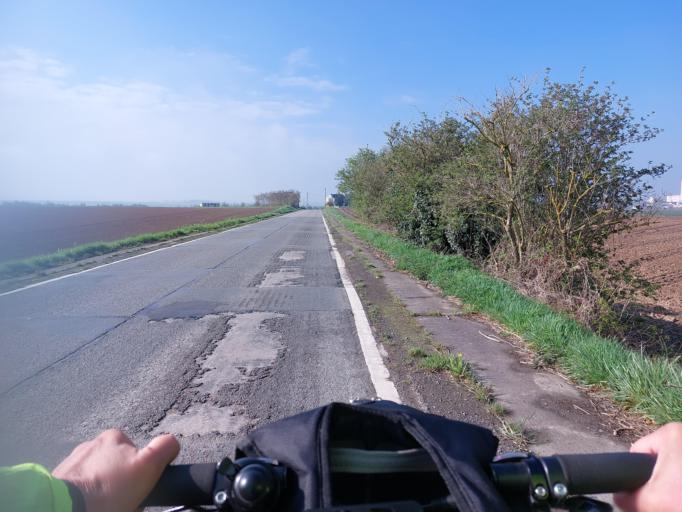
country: BE
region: Wallonia
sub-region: Province du Hainaut
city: Estinnes-au-Val
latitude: 50.4165
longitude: 4.0299
